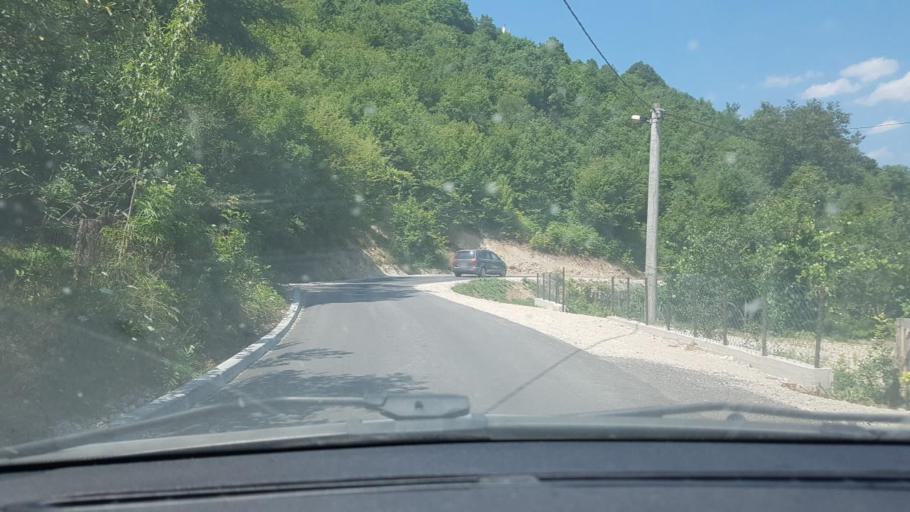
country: BA
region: Federation of Bosnia and Herzegovina
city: Orasac
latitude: 44.6235
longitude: 16.0656
